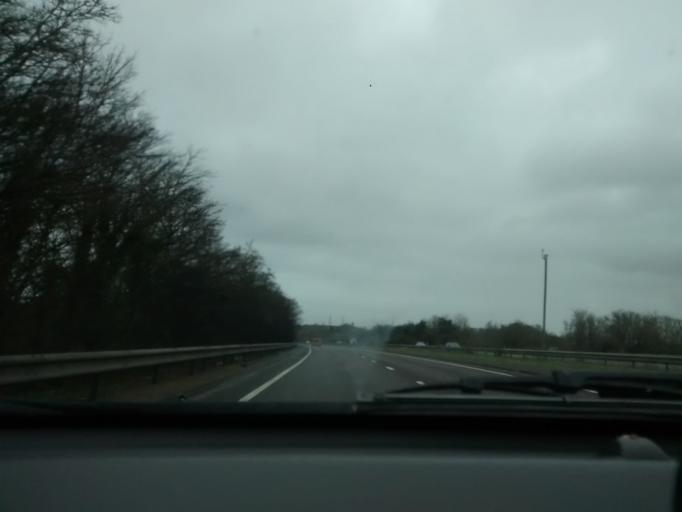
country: GB
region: England
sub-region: Suffolk
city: Bramford
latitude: 52.1050
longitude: 1.1070
